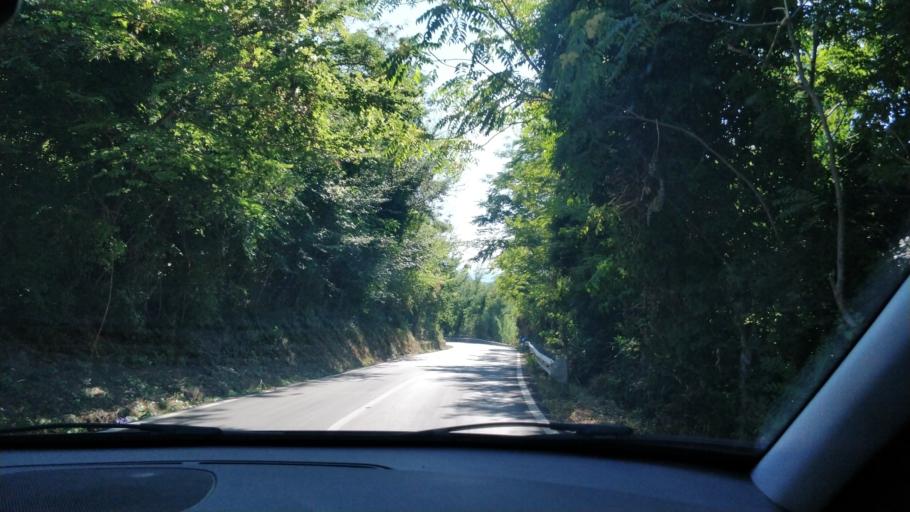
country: IT
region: Abruzzo
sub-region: Provincia di Pescara
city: Serramonacesca
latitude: 42.2545
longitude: 14.0864
